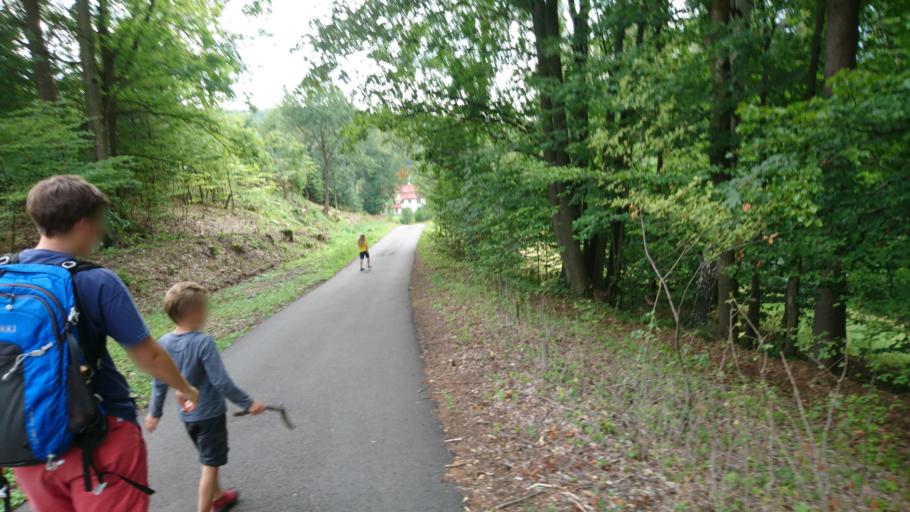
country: CZ
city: Novy Bor
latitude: 50.8074
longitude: 14.5436
